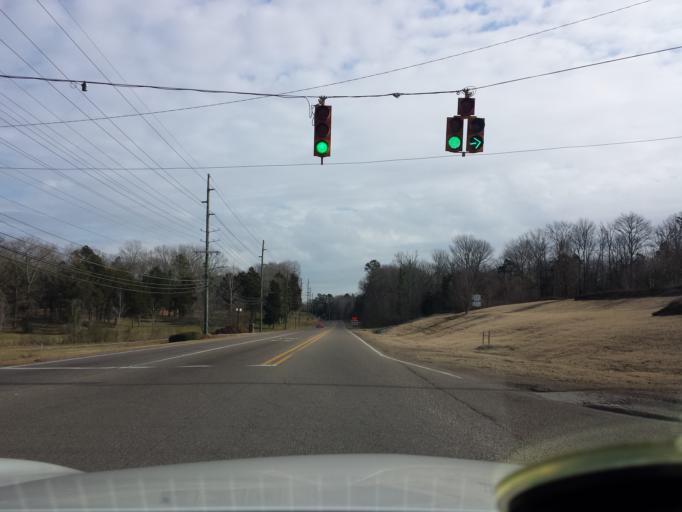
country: US
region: Mississippi
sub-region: Oktibbeha County
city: Starkville
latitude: 33.4620
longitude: -88.8453
